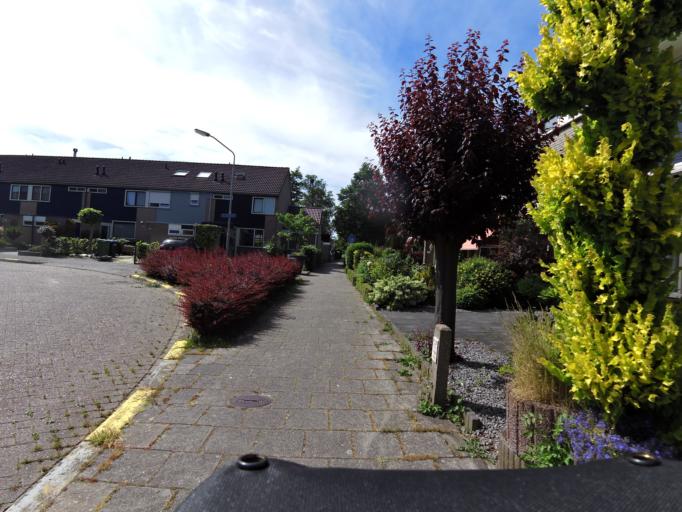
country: NL
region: North Brabant
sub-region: Gemeente Moerdijk
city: Willemstad
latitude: 51.6878
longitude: 4.4422
